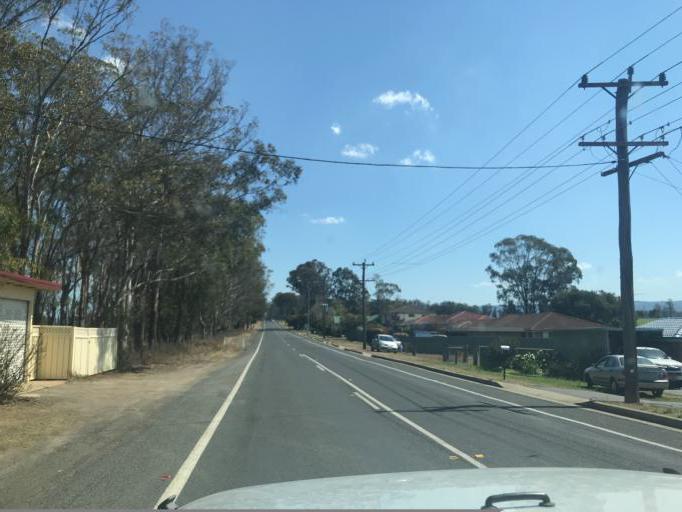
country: AU
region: New South Wales
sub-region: Hawkesbury
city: Richmond
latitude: -33.5640
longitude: 150.7564
